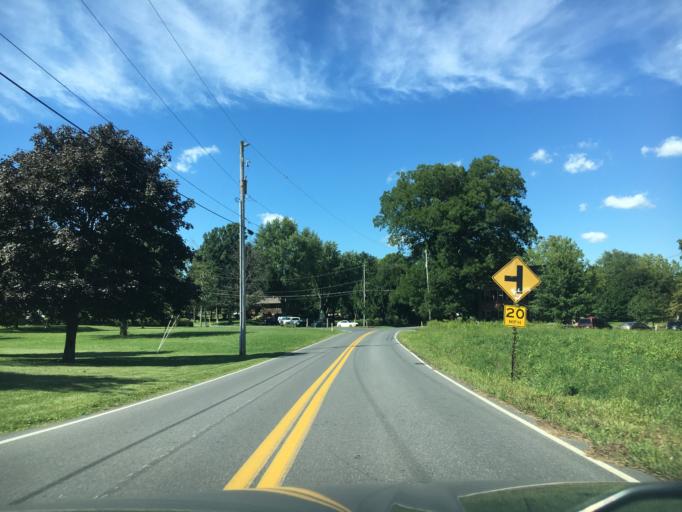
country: US
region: Pennsylvania
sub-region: Berks County
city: Topton
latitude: 40.5157
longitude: -75.6892
